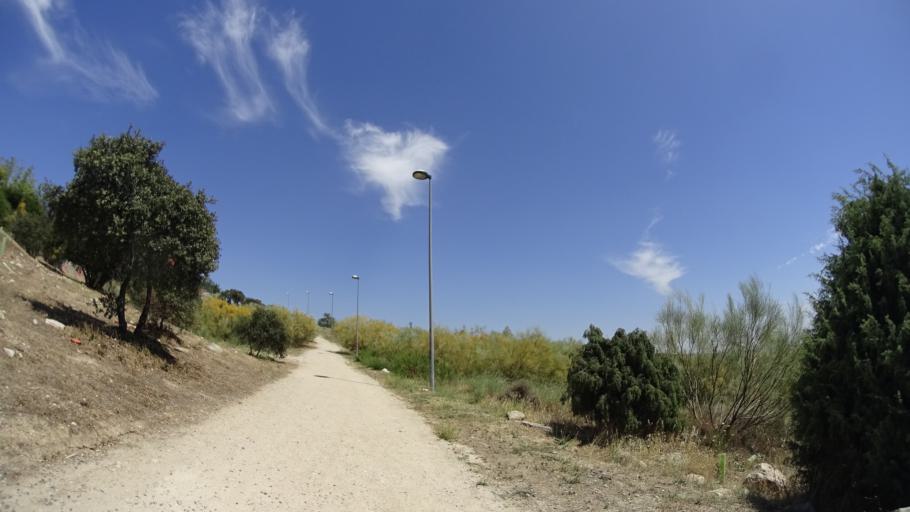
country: ES
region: Madrid
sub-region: Provincia de Madrid
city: Torrelodones
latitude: 40.5689
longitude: -3.9234
